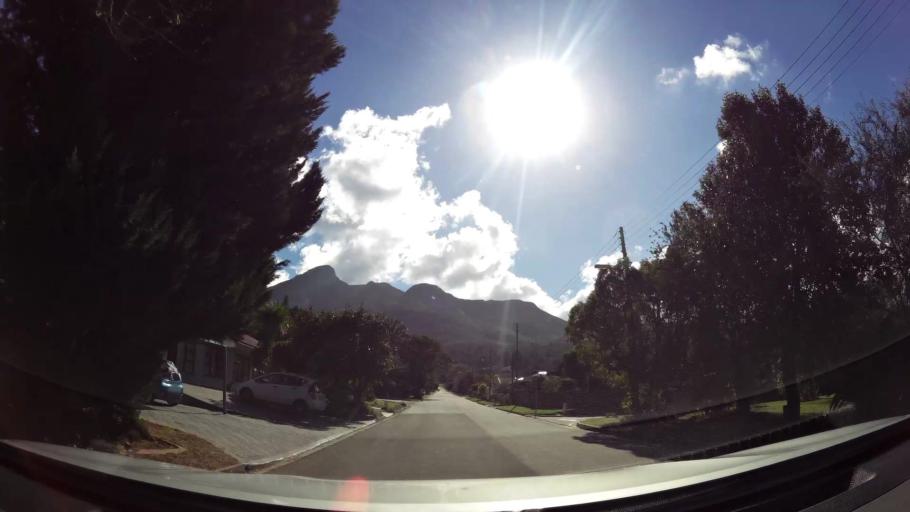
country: ZA
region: Western Cape
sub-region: Eden District Municipality
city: George
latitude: -33.9415
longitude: 22.4760
